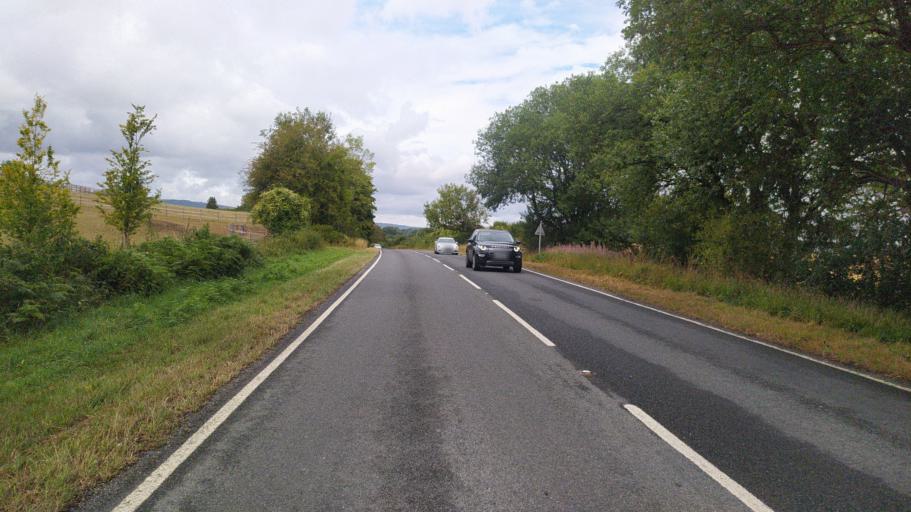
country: GB
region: England
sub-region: Hampshire
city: Petersfield
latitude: 50.9728
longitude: -0.8978
